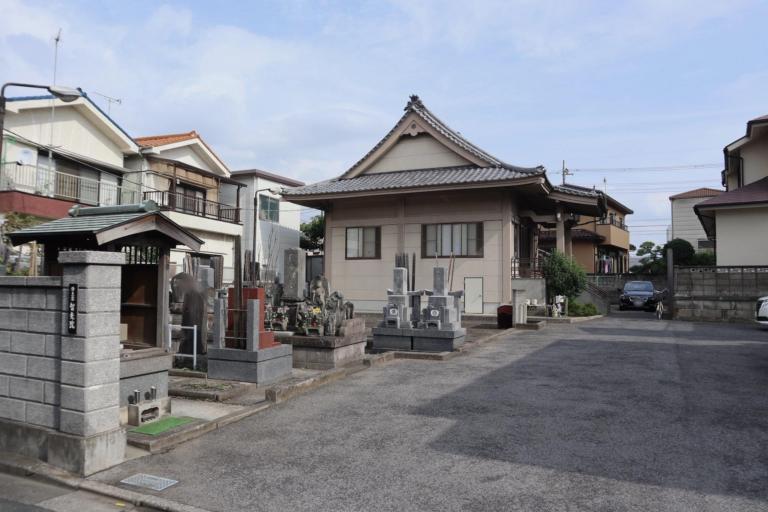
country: JP
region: Tokyo
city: Urayasu
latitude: 35.6692
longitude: 139.8830
